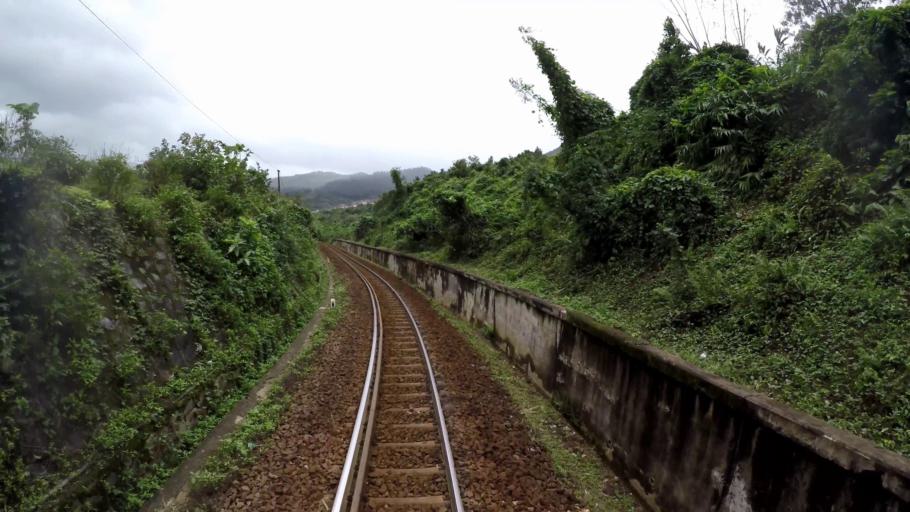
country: VN
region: Da Nang
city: Lien Chieu
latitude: 16.1710
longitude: 108.1367
